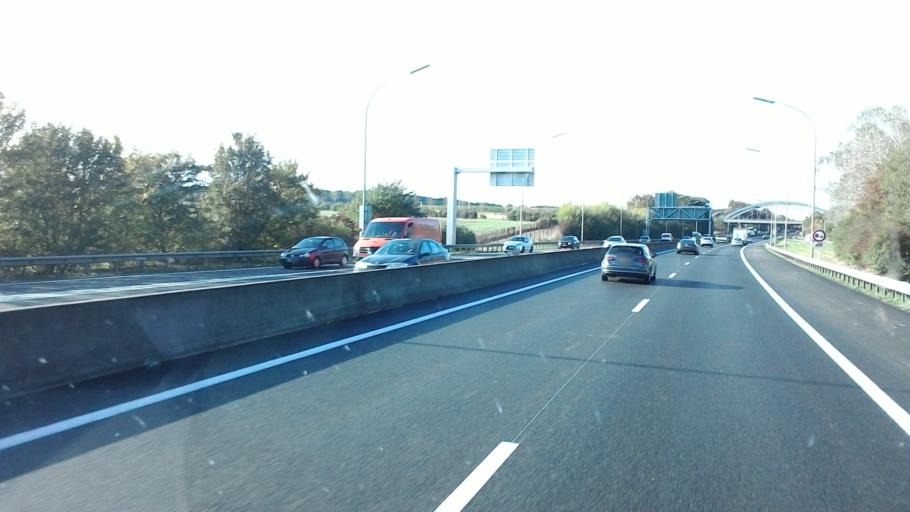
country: LU
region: Luxembourg
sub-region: Canton d'Esch-sur-Alzette
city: Leudelange
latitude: 49.5871
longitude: 6.0859
